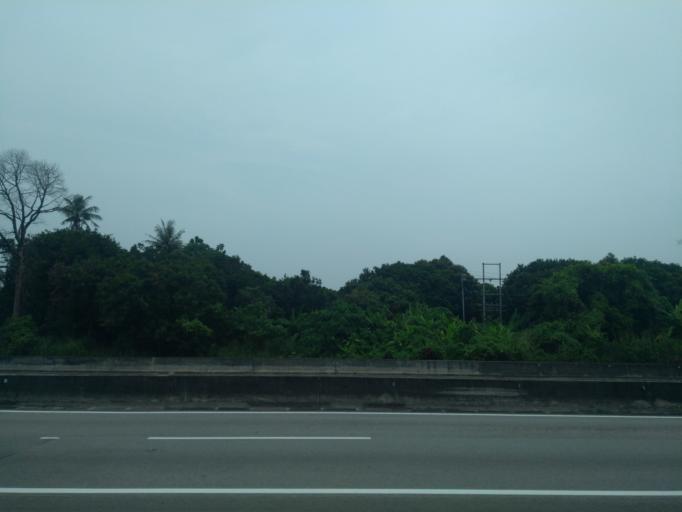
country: MY
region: Perak
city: Ipoh
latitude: 4.6260
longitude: 101.1108
